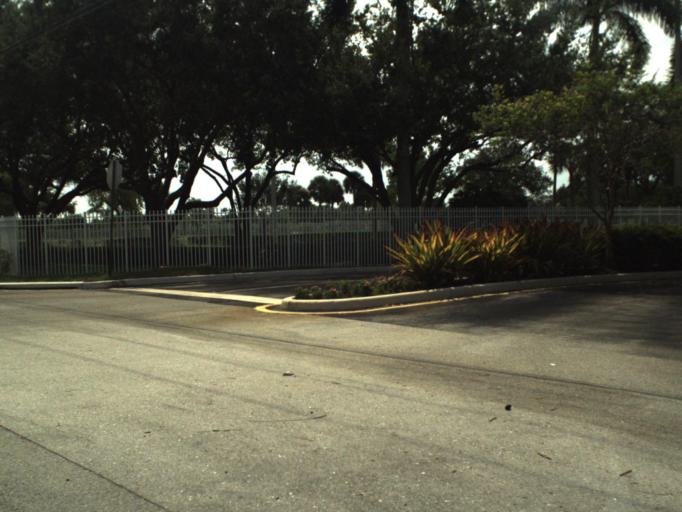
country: US
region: Florida
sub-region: Broward County
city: Palm Aire
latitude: 26.2026
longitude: -80.1744
